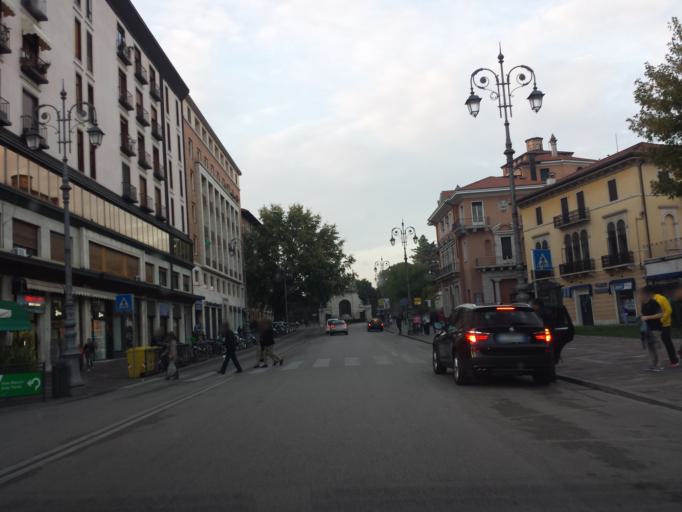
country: IT
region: Veneto
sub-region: Provincia di Vicenza
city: Vicenza
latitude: 45.5447
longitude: 11.5404
